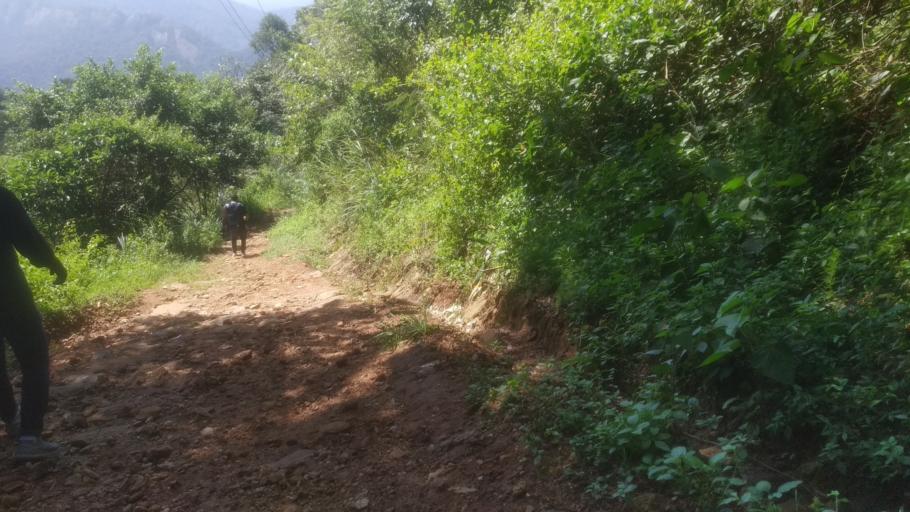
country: IN
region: Kerala
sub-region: Idukki
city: Idukki
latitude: 9.9761
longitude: 76.8375
